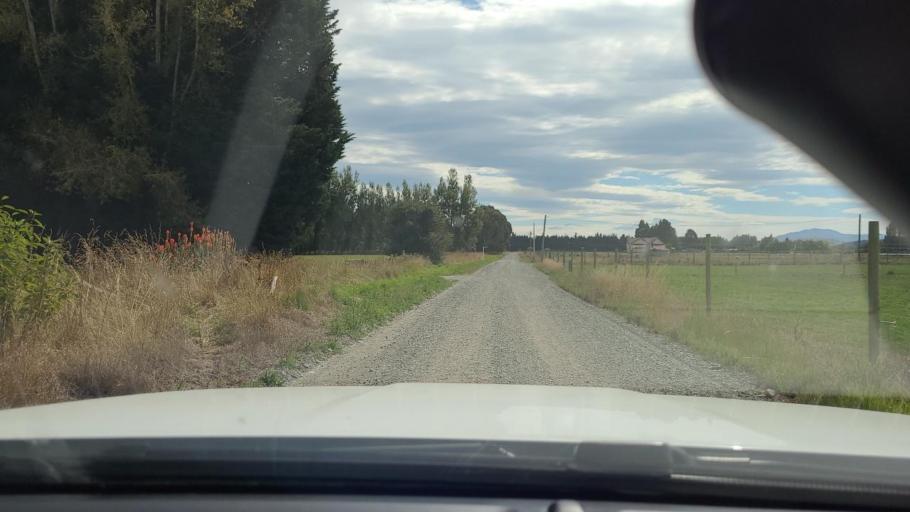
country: NZ
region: Southland
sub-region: Southland District
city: Winton
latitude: -45.8899
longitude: 168.3552
